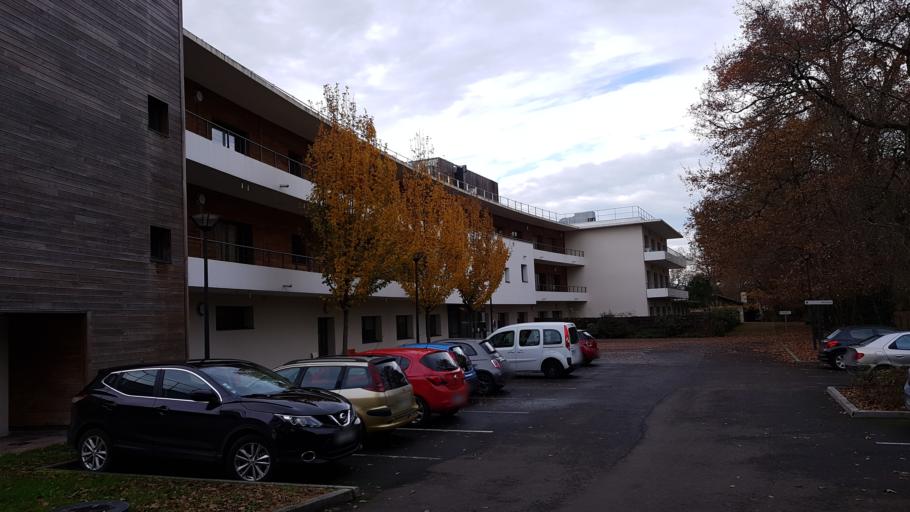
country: FR
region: Aquitaine
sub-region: Departement des Landes
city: Saint-Paul-les-Dax
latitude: 43.7343
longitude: -1.0559
